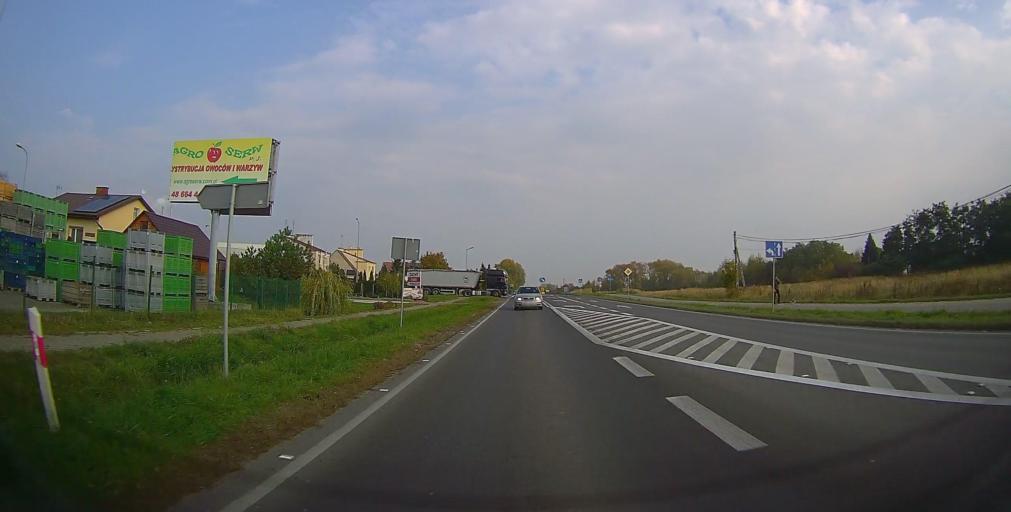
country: PL
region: Masovian Voivodeship
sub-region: Powiat grojecki
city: Mogielnica
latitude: 51.7373
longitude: 20.7569
